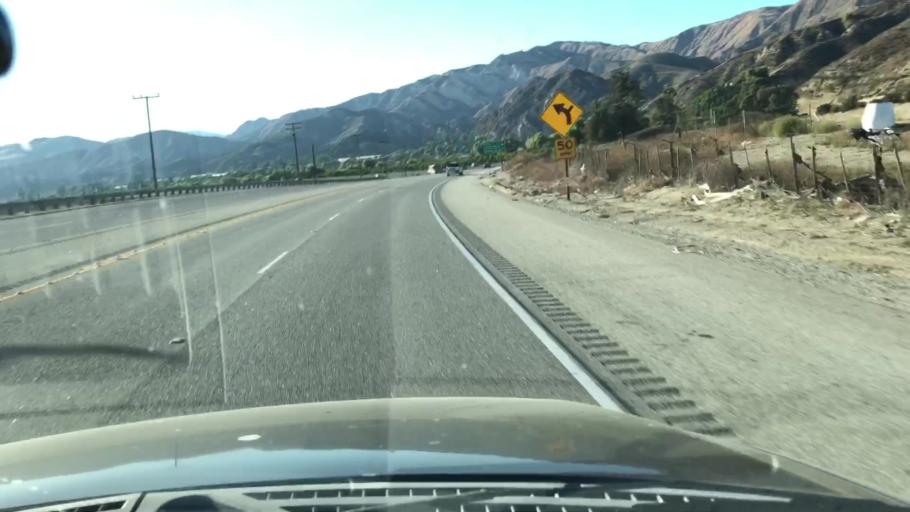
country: US
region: California
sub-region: Ventura County
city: Piru
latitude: 34.4091
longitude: -118.7777
